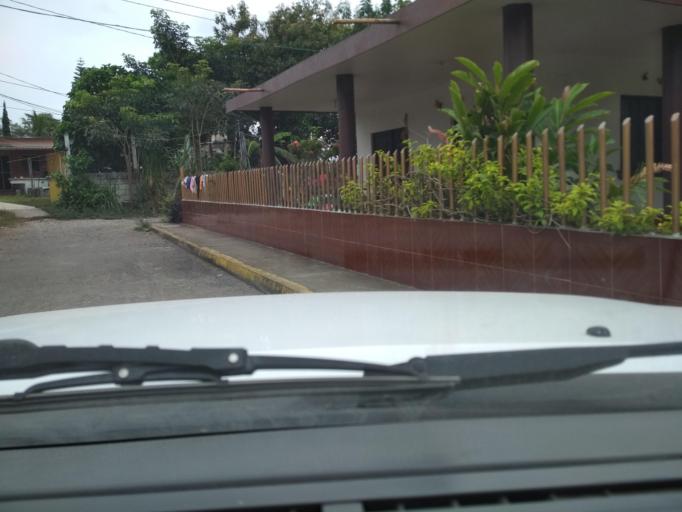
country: MX
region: Veracruz
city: Paso del Toro
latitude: 19.0550
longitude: -96.1373
